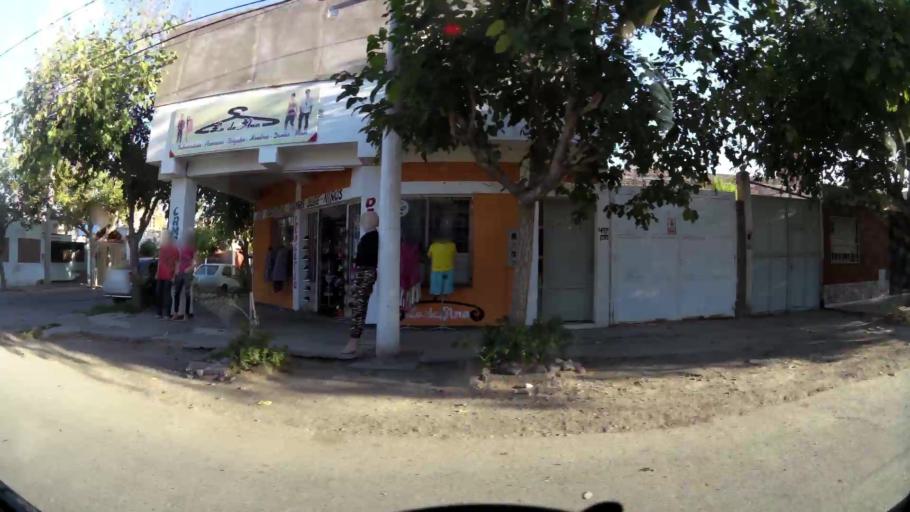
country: AR
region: San Juan
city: San Juan
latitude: -31.5447
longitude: -68.5177
